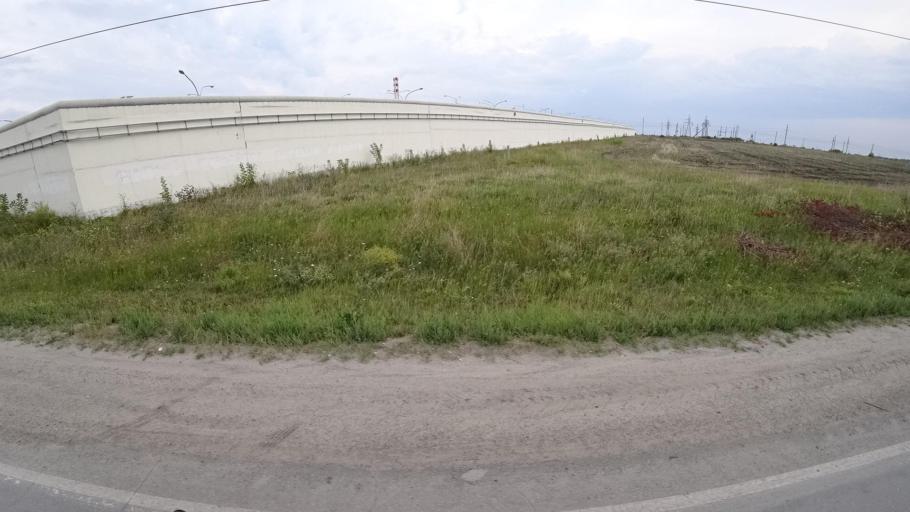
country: RU
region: Sverdlovsk
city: Kamyshlov
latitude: 56.8543
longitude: 62.7361
